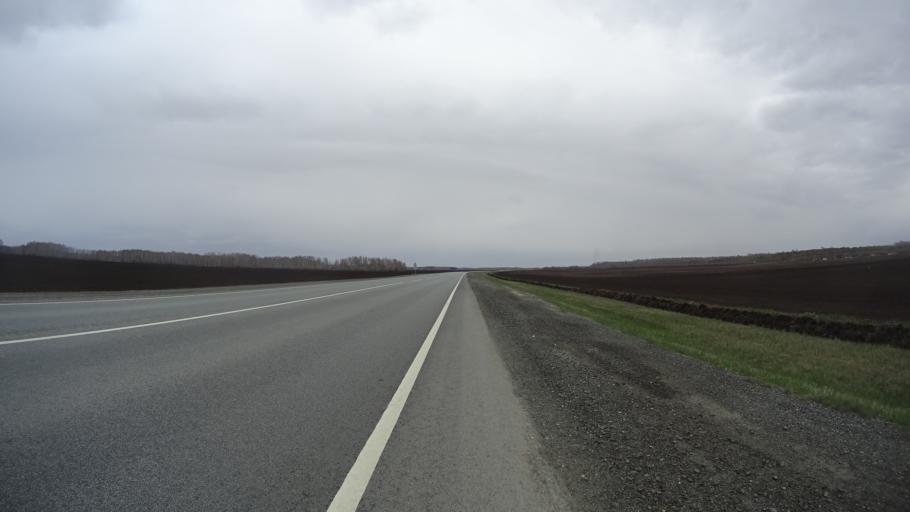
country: RU
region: Chelyabinsk
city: Krasnogorskiy
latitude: 54.5799
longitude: 61.2913
